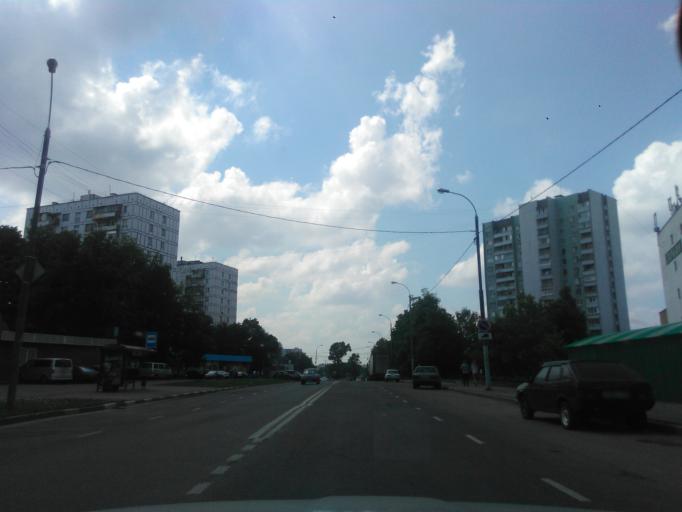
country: RU
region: Moscow
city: Businovo
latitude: 55.8849
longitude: 37.5210
